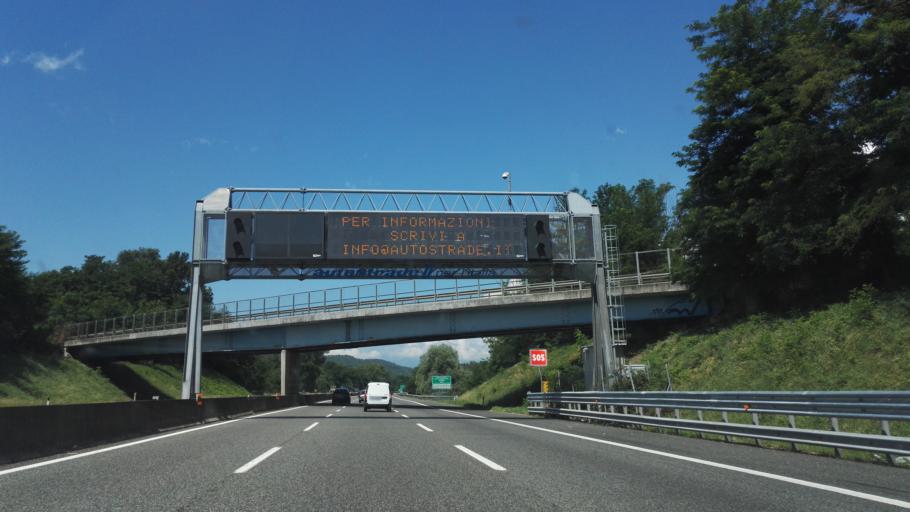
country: IT
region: Piedmont
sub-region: Provincia di Novara
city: Borgo Ticino
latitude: 45.6988
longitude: 8.6192
